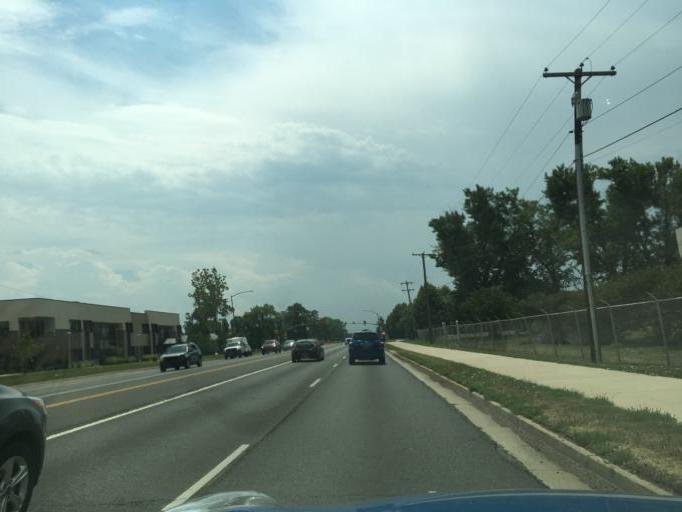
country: US
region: Colorado
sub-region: Jefferson County
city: Wheat Ridge
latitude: 39.7602
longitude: -105.0816
